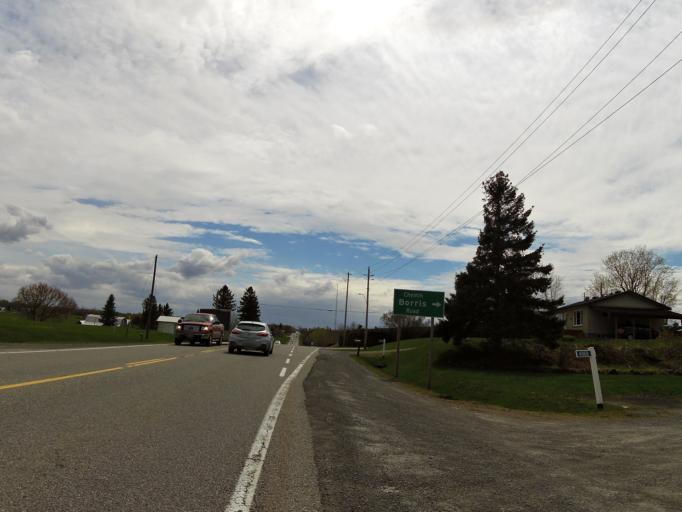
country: CA
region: Ontario
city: Hawkesbury
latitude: 45.5374
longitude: -74.6429
